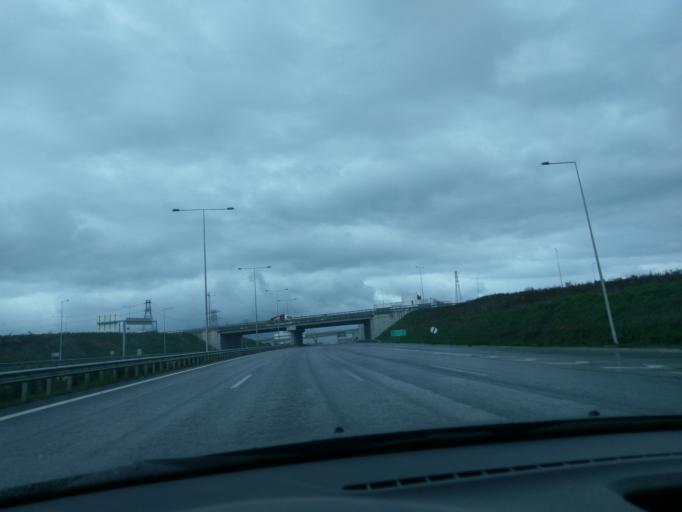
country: TR
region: Istanbul
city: Basaksehir
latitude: 41.1369
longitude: 28.8050
